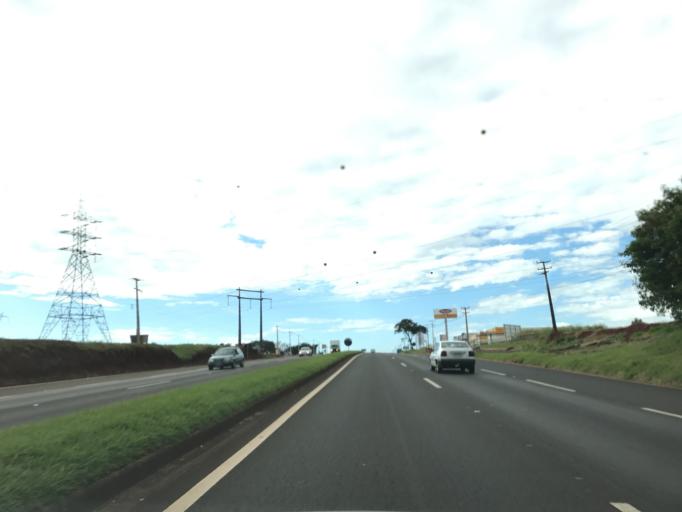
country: BR
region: Parana
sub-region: Sarandi
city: Sarandi
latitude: -23.4550
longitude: -51.8478
